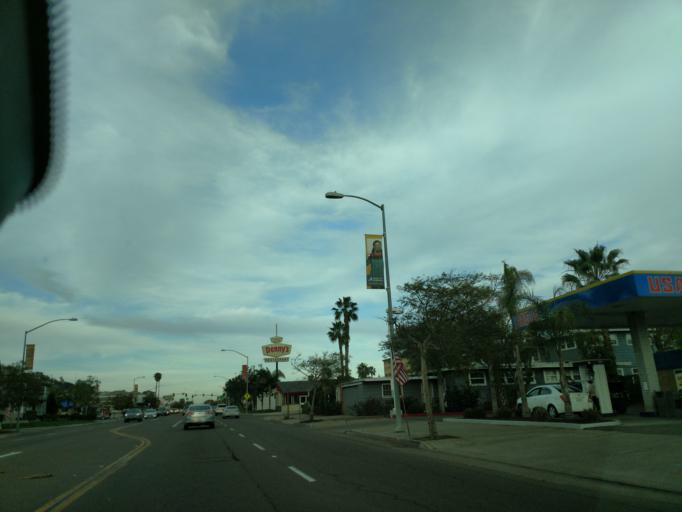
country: US
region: California
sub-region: San Diego County
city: Coronado
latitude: 32.7268
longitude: -117.2273
